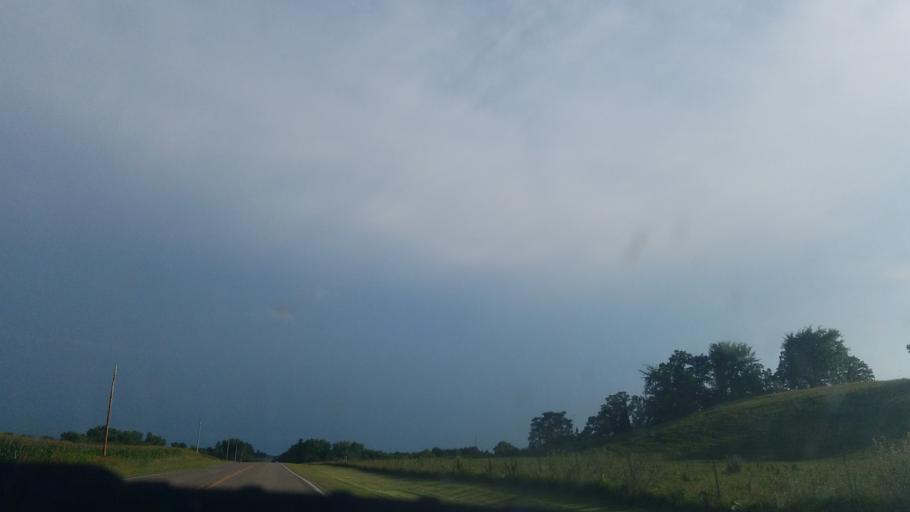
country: US
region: Wisconsin
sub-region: Dunn County
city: Menomonie
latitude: 44.8190
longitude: -91.8934
